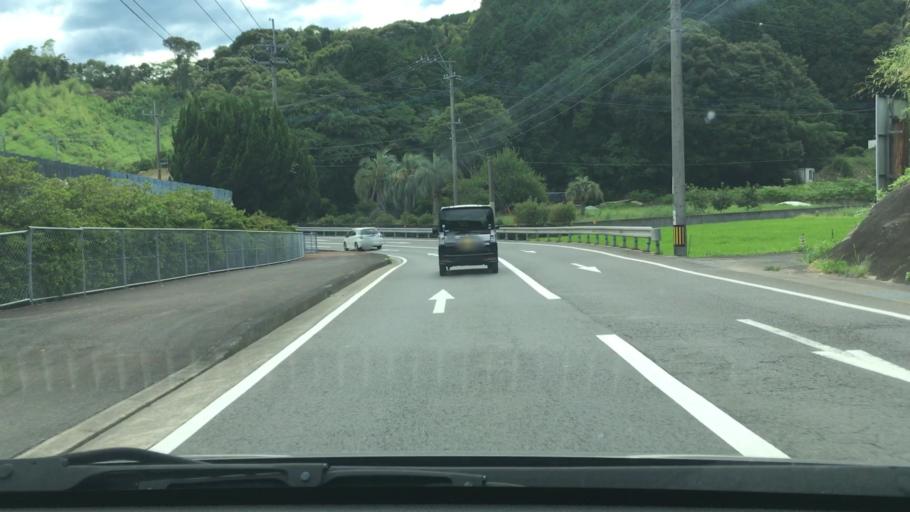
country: JP
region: Nagasaki
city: Togitsu
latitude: 32.9193
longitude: 129.7861
